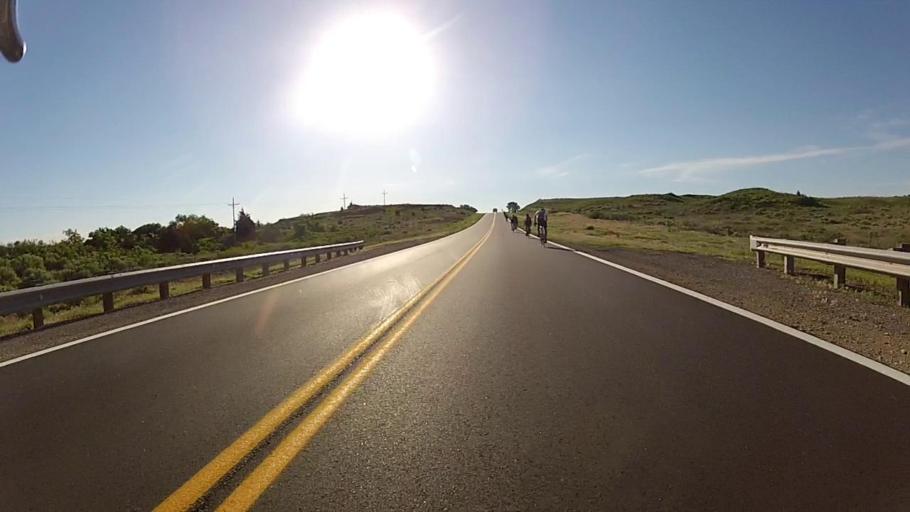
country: US
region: Kansas
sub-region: Comanche County
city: Coldwater
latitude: 37.2809
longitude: -99.0327
